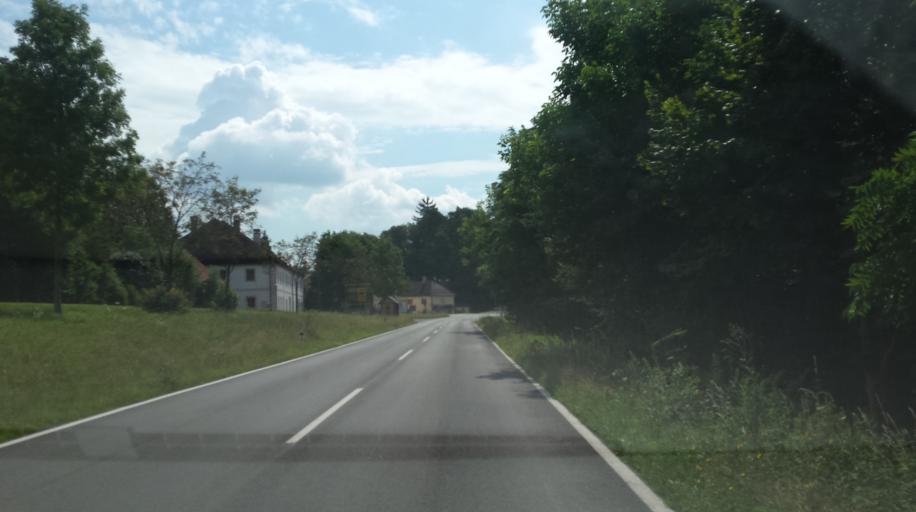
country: AT
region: Lower Austria
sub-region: Politischer Bezirk Amstetten
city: Haag
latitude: 48.1032
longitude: 14.5569
